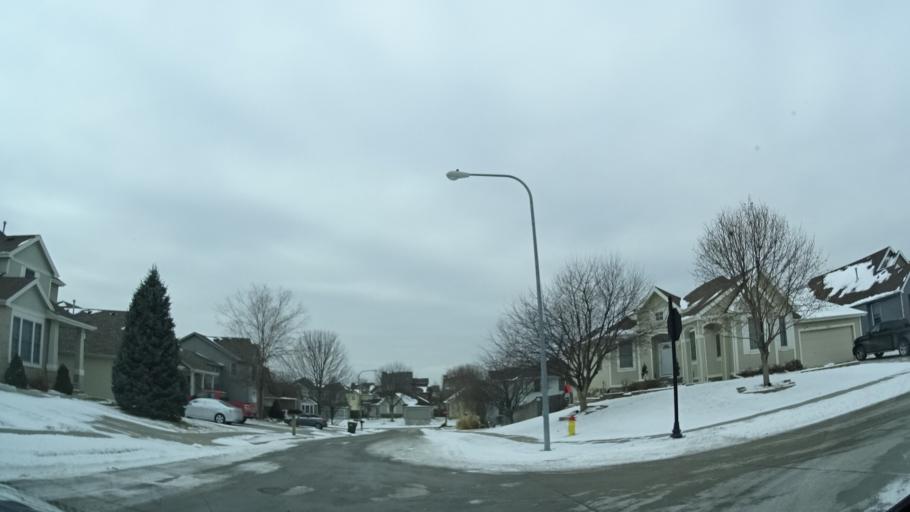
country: US
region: Nebraska
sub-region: Sarpy County
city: Offutt Air Force Base
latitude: 41.1633
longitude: -95.9517
